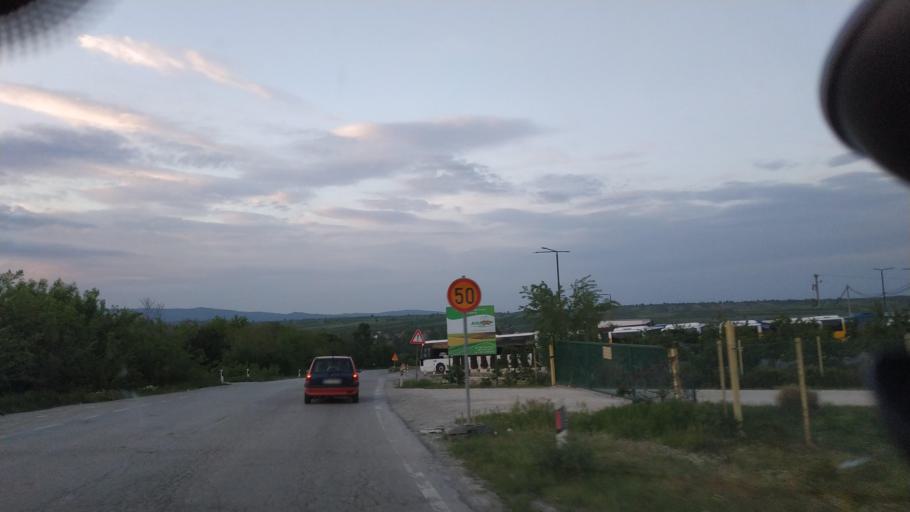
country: RS
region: Central Serbia
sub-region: Toplicki Okrug
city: Prokuplje
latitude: 43.2534
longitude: 21.6469
